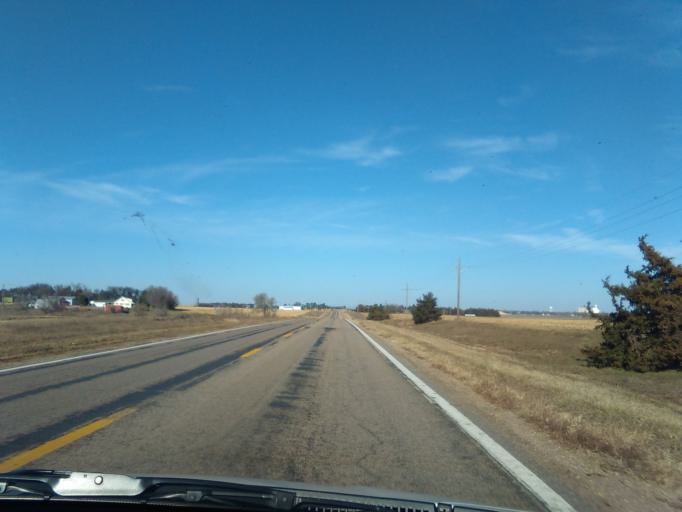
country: US
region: Nebraska
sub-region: Clay County
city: Harvard
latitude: 40.5906
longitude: -98.1091
